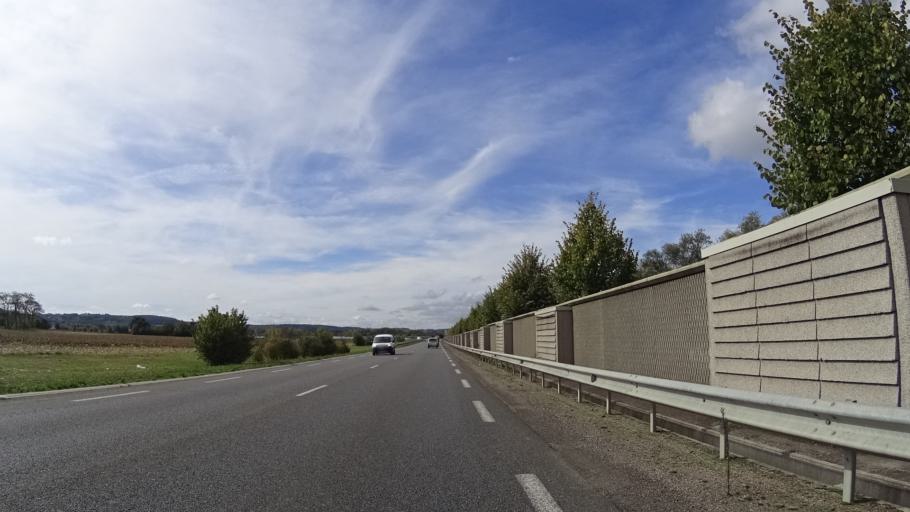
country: FR
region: Aquitaine
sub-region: Departement du Lot-et-Garonne
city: Boe
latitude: 44.1748
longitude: 0.6420
